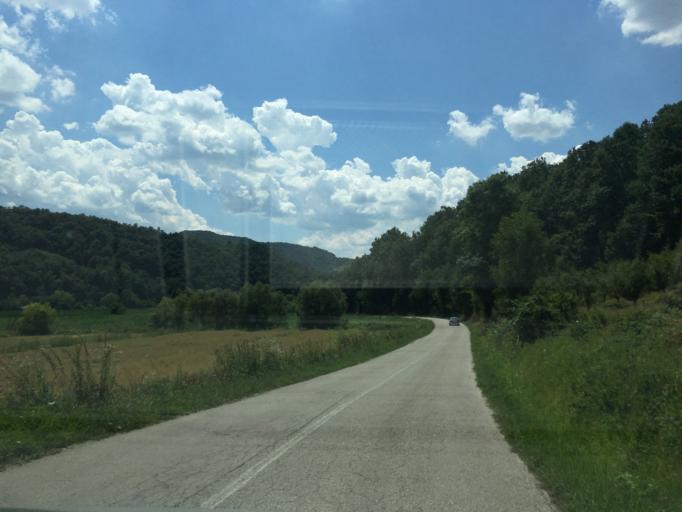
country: RS
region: Central Serbia
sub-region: Kolubarski Okrug
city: Ljig
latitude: 44.2405
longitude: 20.3589
